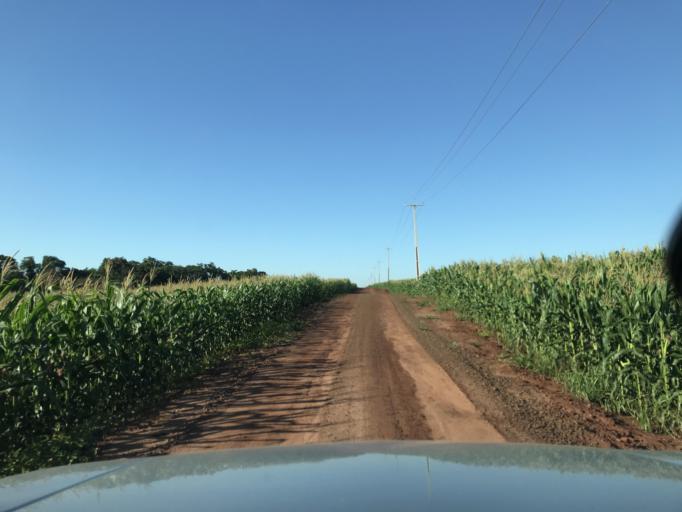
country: BR
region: Parana
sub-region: Palotina
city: Palotina
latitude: -24.2107
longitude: -53.7485
